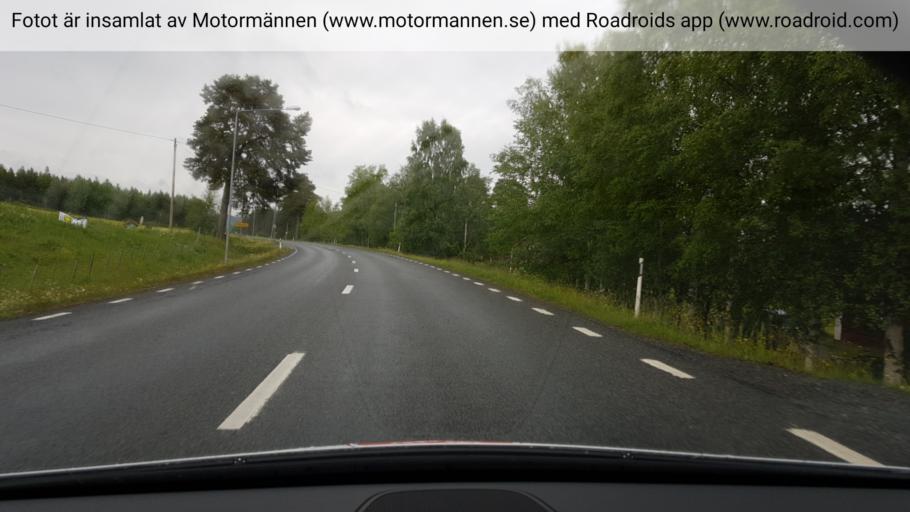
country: SE
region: Jaemtland
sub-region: OEstersunds Kommun
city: Lit
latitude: 63.3908
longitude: 14.9614
